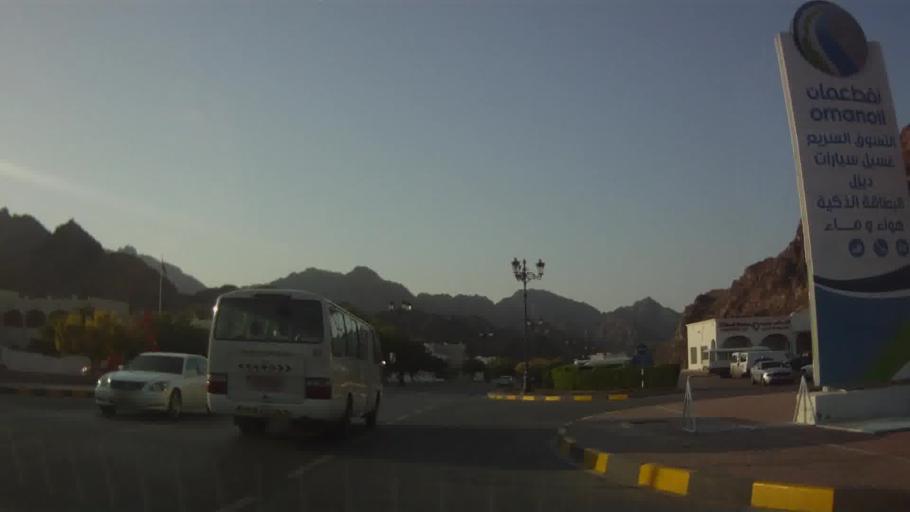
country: OM
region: Muhafazat Masqat
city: Muscat
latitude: 23.5900
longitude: 58.5995
